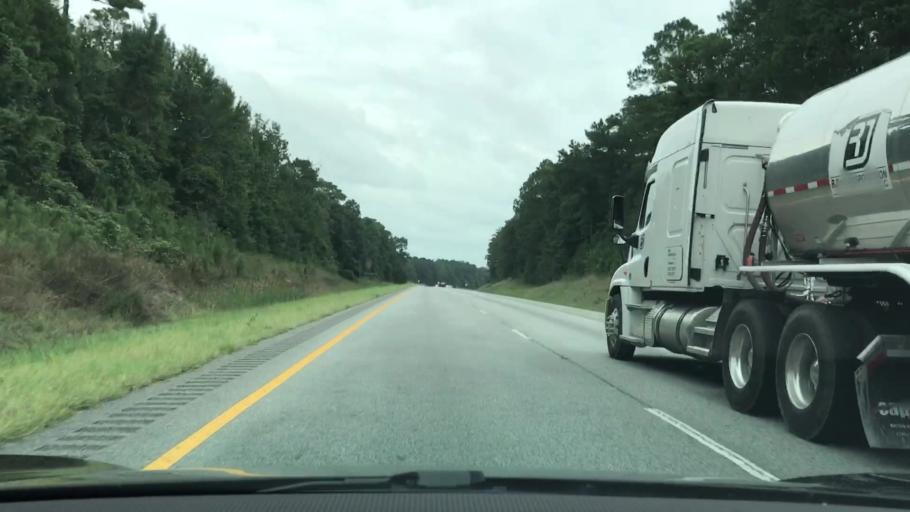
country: US
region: Alabama
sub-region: Macon County
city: Tuskegee
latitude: 32.5029
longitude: -85.6096
